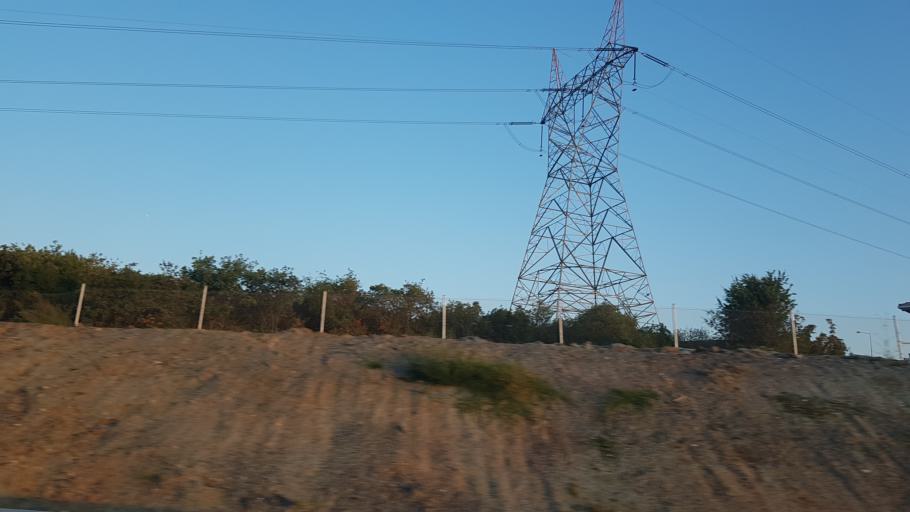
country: TR
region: Kocaeli
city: Tavsanli
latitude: 40.8013
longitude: 29.5188
